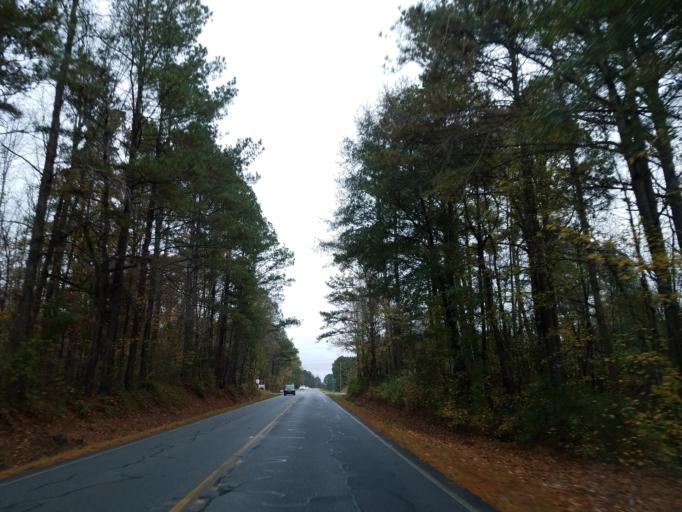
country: US
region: Georgia
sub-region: Cherokee County
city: Canton
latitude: 34.3238
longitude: -84.5444
